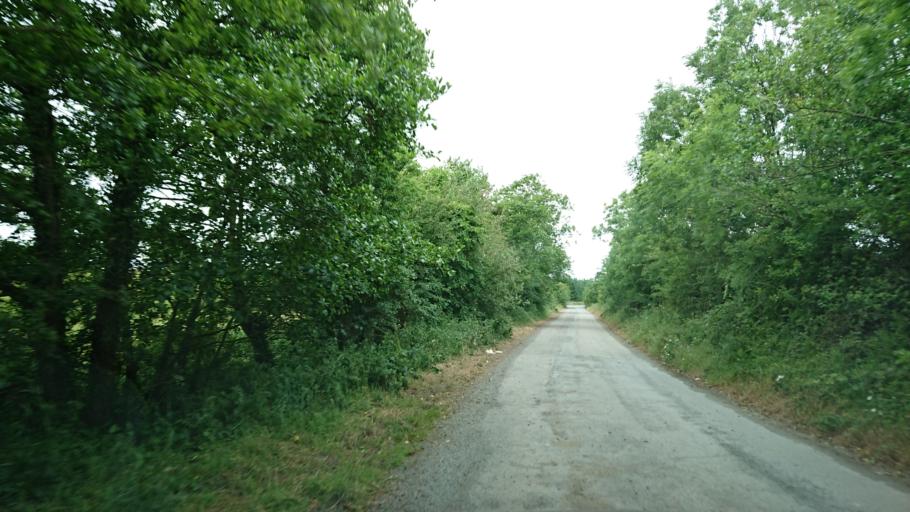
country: IE
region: Munster
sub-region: Waterford
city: Waterford
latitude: 52.2179
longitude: -7.1373
